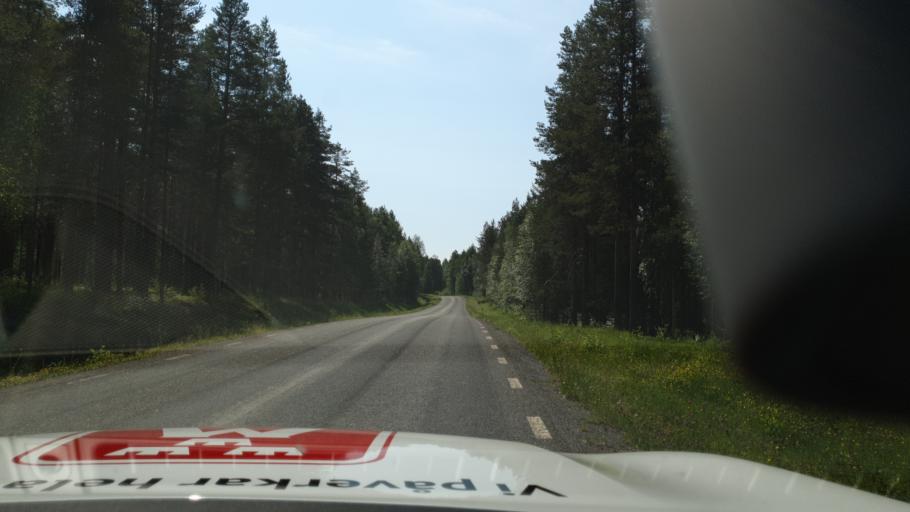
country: SE
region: Vaesterbotten
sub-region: Skelleftea Kommun
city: Langsele
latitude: 65.0179
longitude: 20.0764
